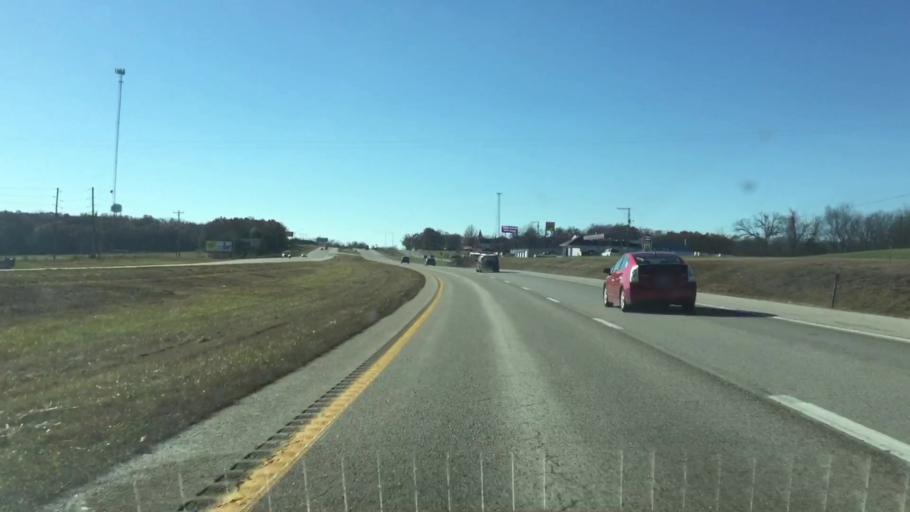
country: US
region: Missouri
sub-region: Cole County
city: Wardsville
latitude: 38.4497
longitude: -92.3020
